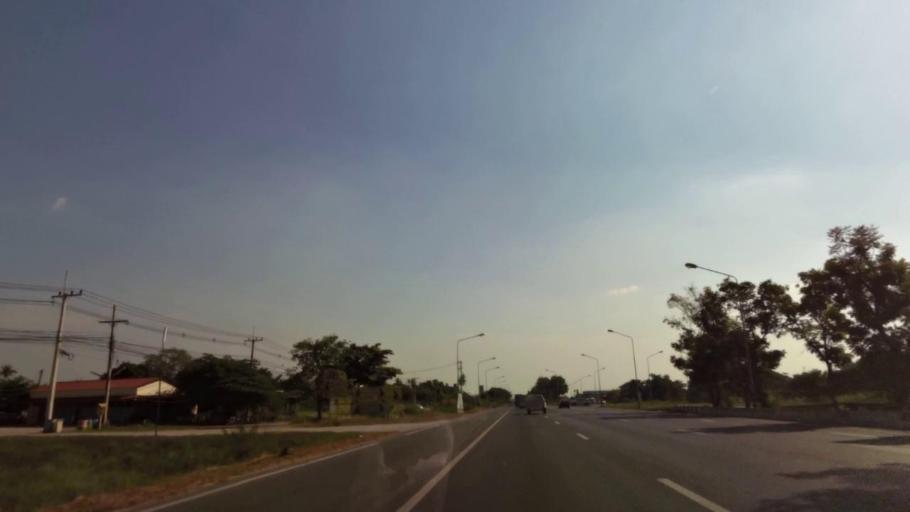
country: TH
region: Ang Thong
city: Chaiyo
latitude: 14.6612
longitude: 100.4726
